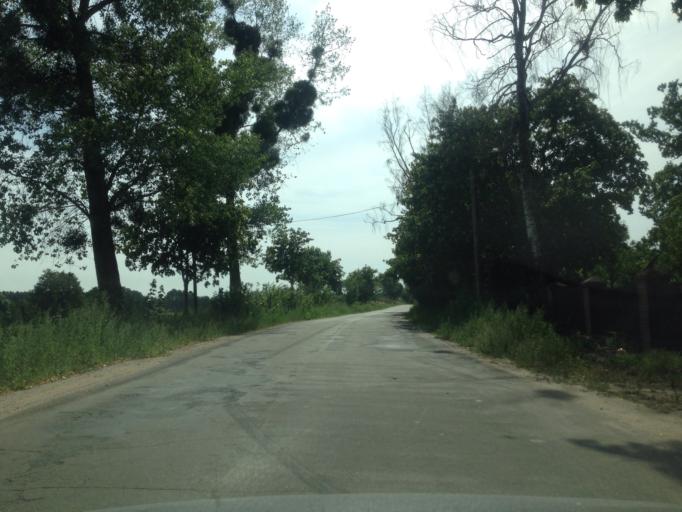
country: PL
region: Kujawsko-Pomorskie
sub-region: Powiat brodnicki
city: Swiedziebnia
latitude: 53.2274
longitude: 19.5117
